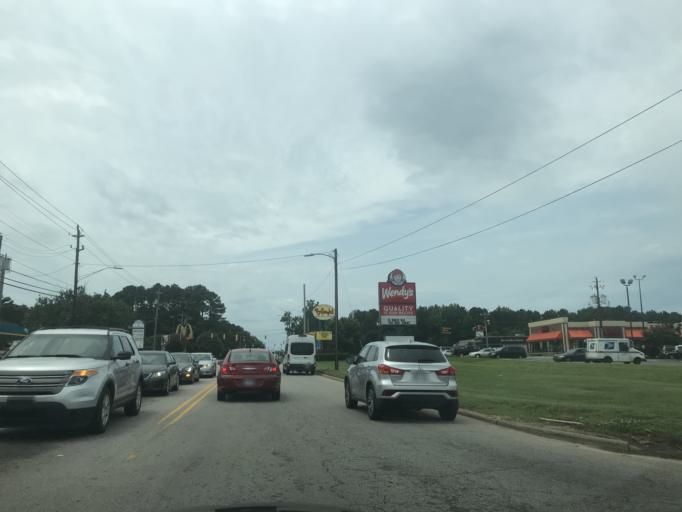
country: US
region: North Carolina
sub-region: Vance County
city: Henderson
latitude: 36.3322
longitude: -78.4344
